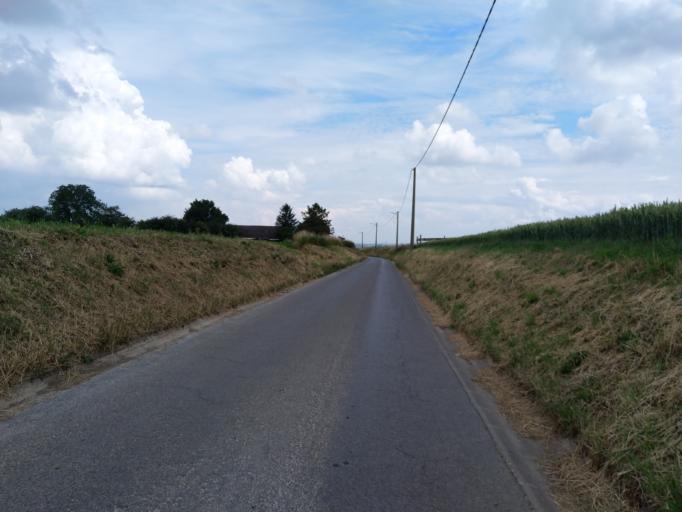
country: FR
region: Nord-Pas-de-Calais
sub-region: Departement du Nord
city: Boussois
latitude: 50.3639
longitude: 4.0273
